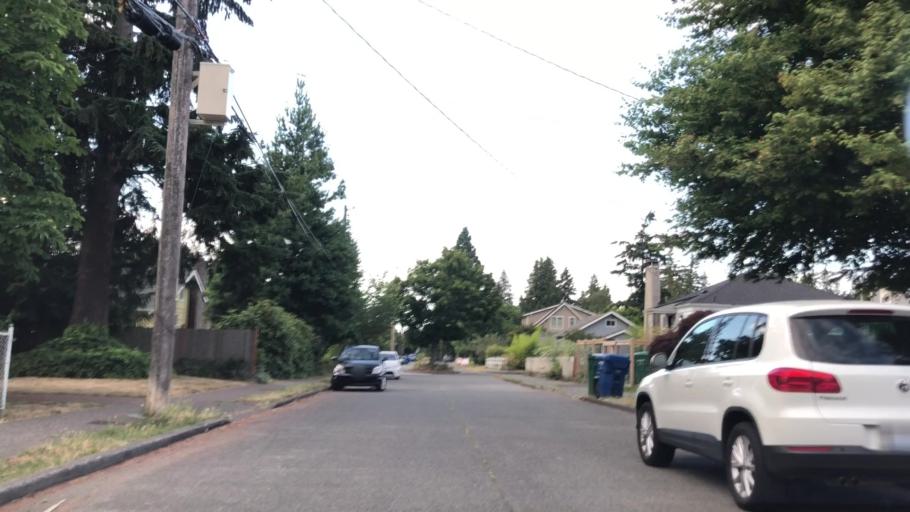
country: US
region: Washington
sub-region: King County
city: Shoreline
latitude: 47.6952
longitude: -122.3149
